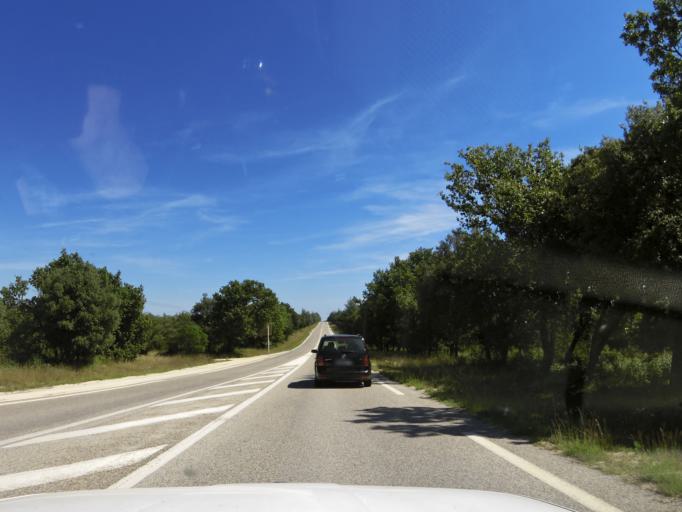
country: FR
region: Languedoc-Roussillon
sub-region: Departement du Gard
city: Saint-Quentin-la-Poterie
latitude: 44.1256
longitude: 4.4600
